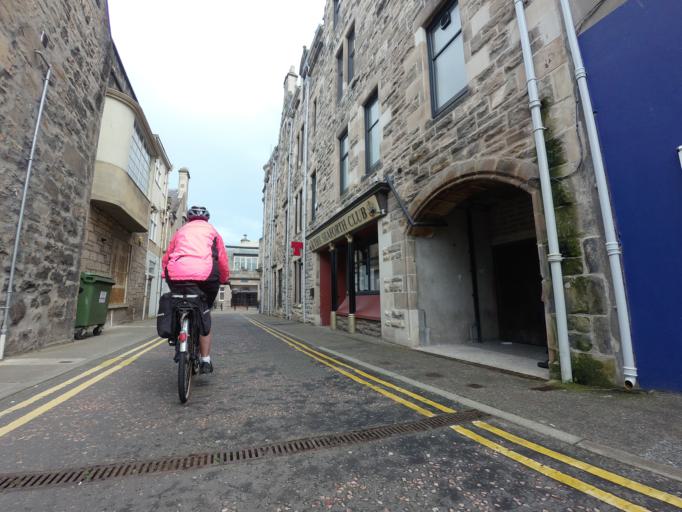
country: GB
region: Scotland
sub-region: Moray
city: Elgin
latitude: 57.6476
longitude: -3.3140
